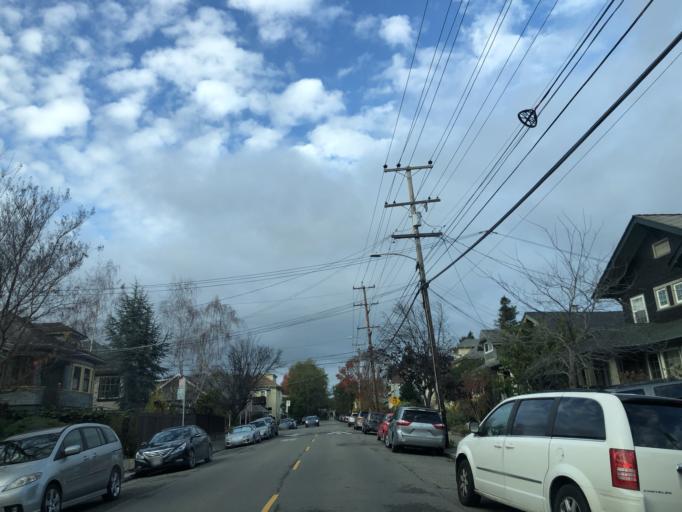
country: US
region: California
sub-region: Alameda County
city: Berkeley
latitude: 37.8479
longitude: -122.2566
